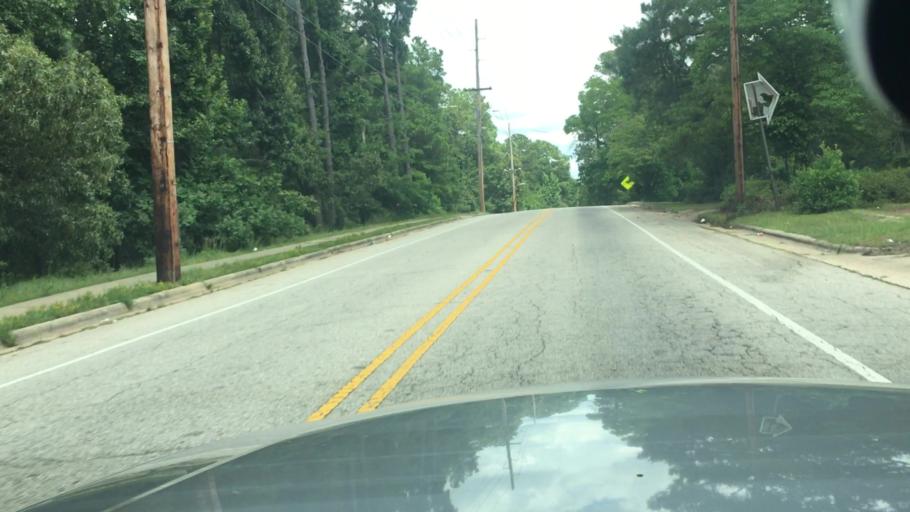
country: US
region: North Carolina
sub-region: Cumberland County
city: Fayetteville
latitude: 35.0674
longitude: -78.9001
